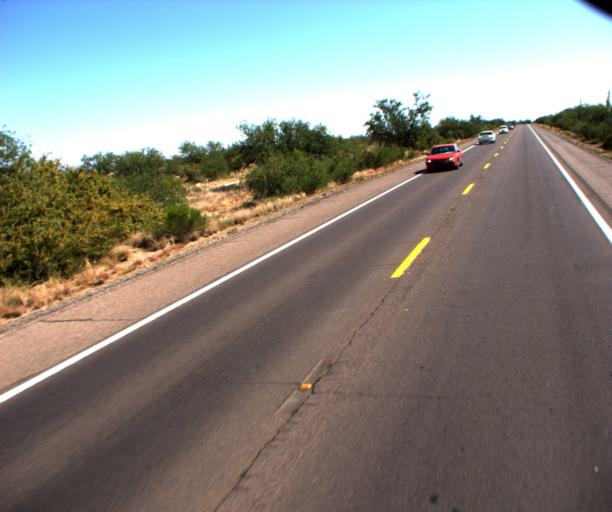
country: US
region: Arizona
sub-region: Pima County
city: Catalina
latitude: 32.5697
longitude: -110.9238
